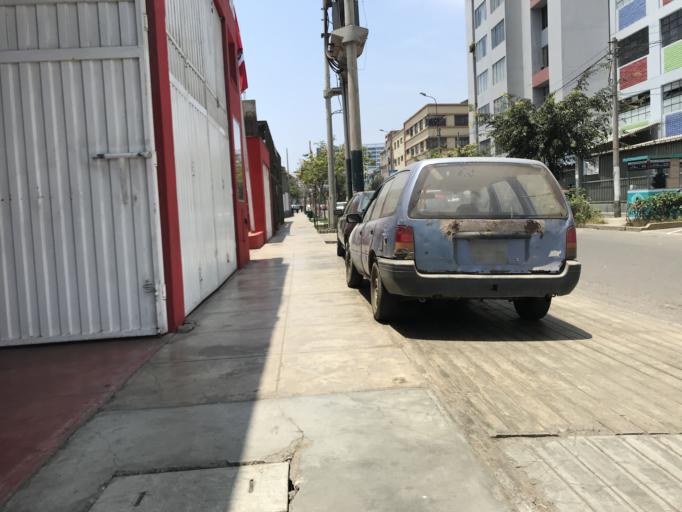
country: PE
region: Lima
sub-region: Lima
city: San Isidro
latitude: -12.0823
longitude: -77.0420
